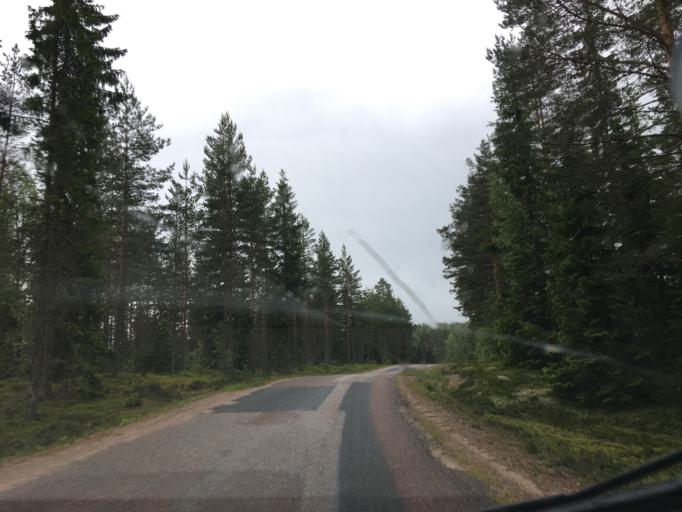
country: SE
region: OErebro
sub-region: Hallefors Kommun
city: Haellefors
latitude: 60.0863
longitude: 14.4848
